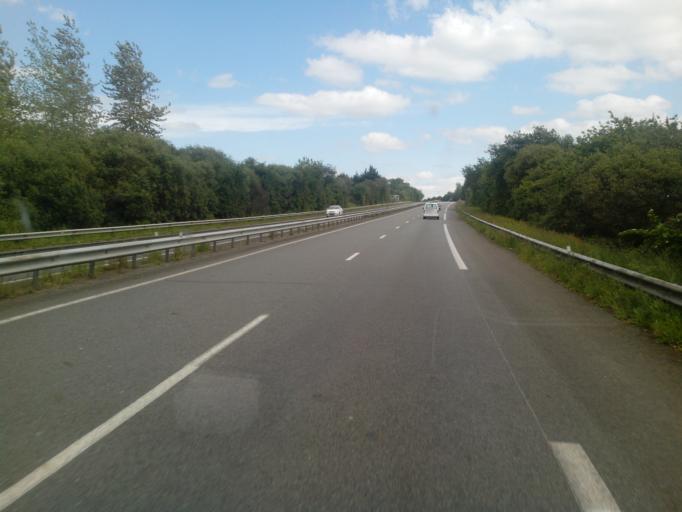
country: FR
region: Brittany
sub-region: Departement des Cotes-d'Armor
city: Pedernec
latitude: 48.5699
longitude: -3.2495
